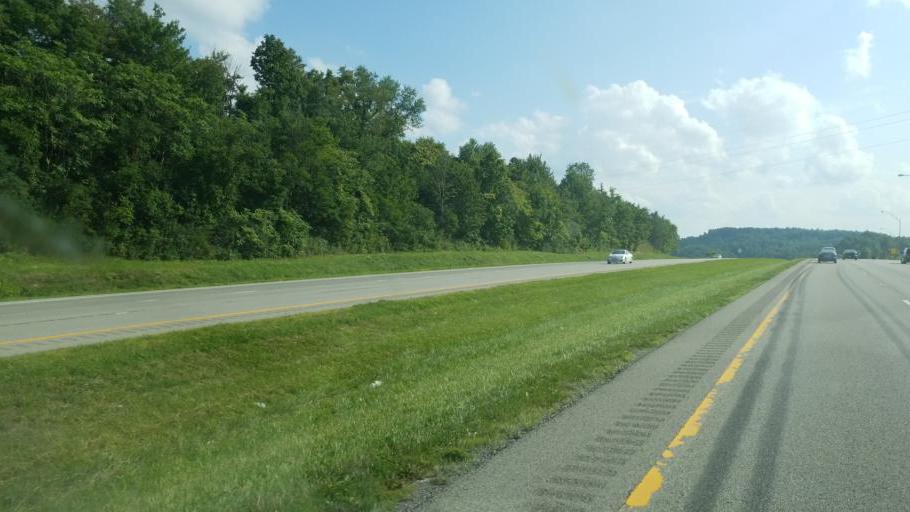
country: US
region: West Virginia
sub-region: Monongalia County
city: Brookhaven
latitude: 39.6514
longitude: -79.8912
